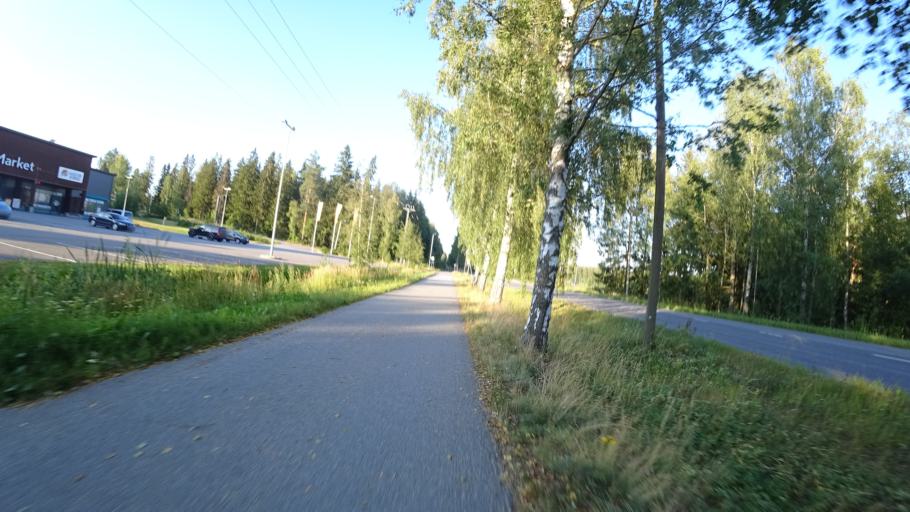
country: FI
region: Pirkanmaa
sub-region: Tampere
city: Nokia
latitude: 61.4718
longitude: 23.4644
